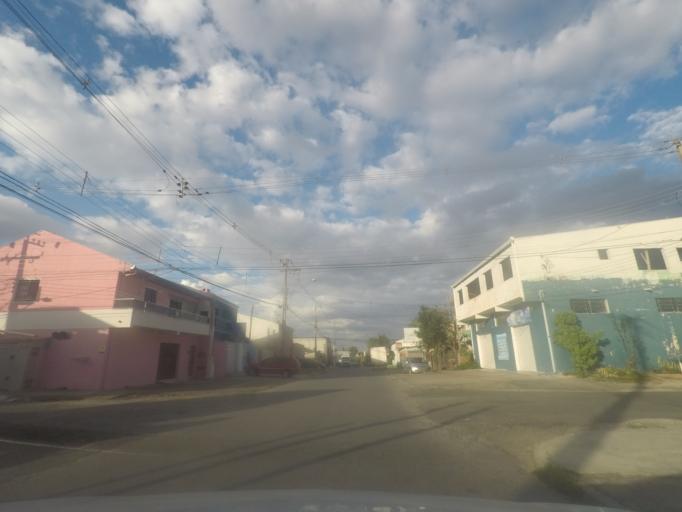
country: BR
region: Parana
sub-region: Pinhais
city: Pinhais
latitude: -25.4635
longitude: -49.2001
